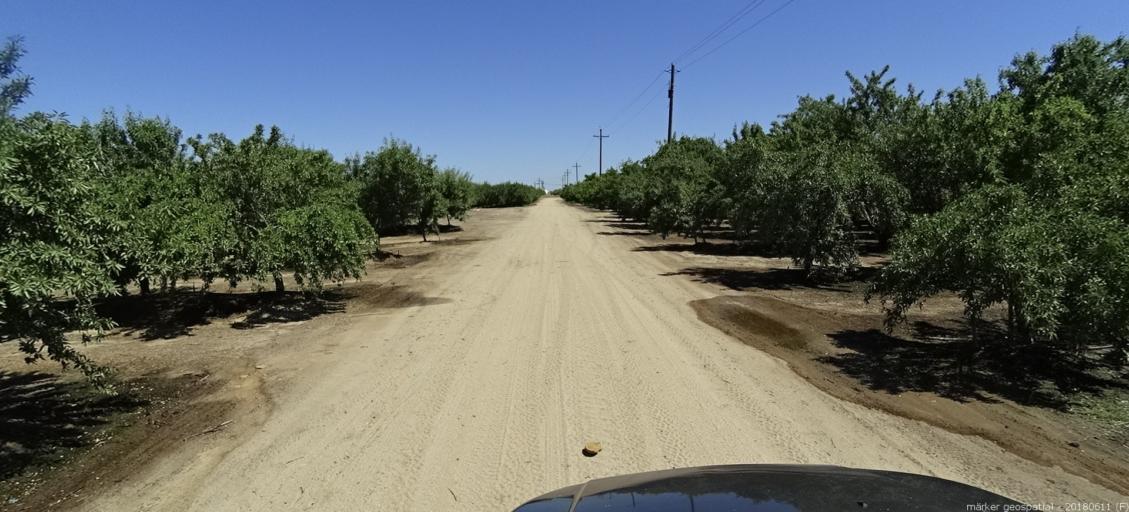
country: US
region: California
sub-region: Madera County
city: Fairmead
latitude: 37.0815
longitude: -120.2205
